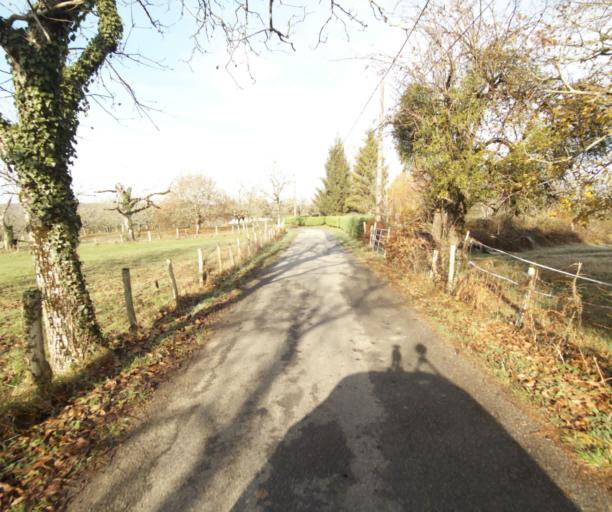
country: FR
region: Limousin
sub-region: Departement de la Correze
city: Sainte-Fortunade
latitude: 45.2236
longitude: 1.7403
